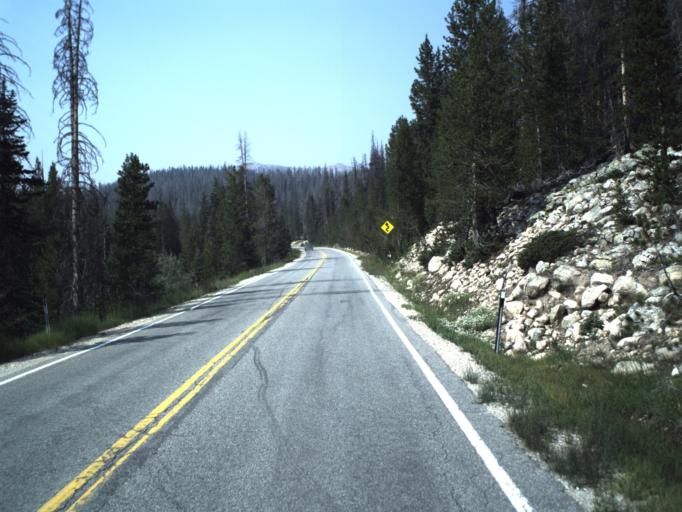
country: US
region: Utah
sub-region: Summit County
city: Kamas
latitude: 40.6642
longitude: -110.9462
